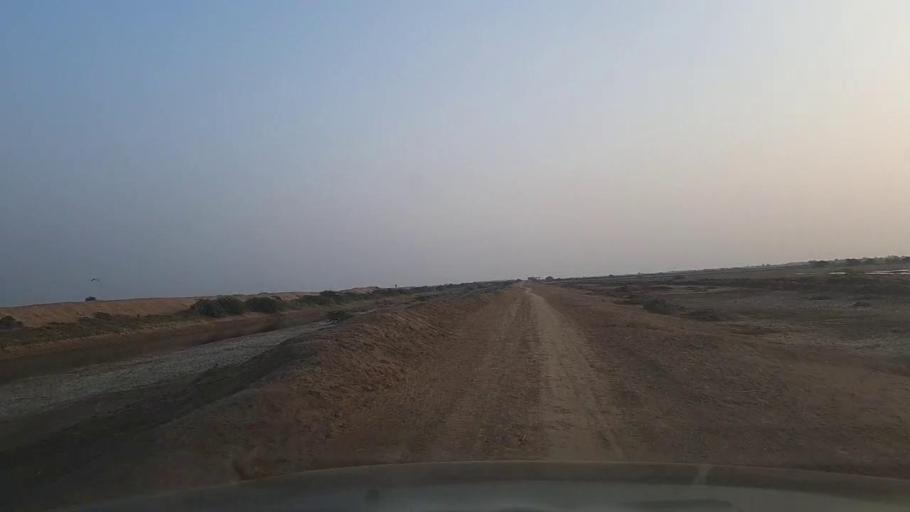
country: PK
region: Sindh
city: Jati
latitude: 24.5357
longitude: 68.4086
